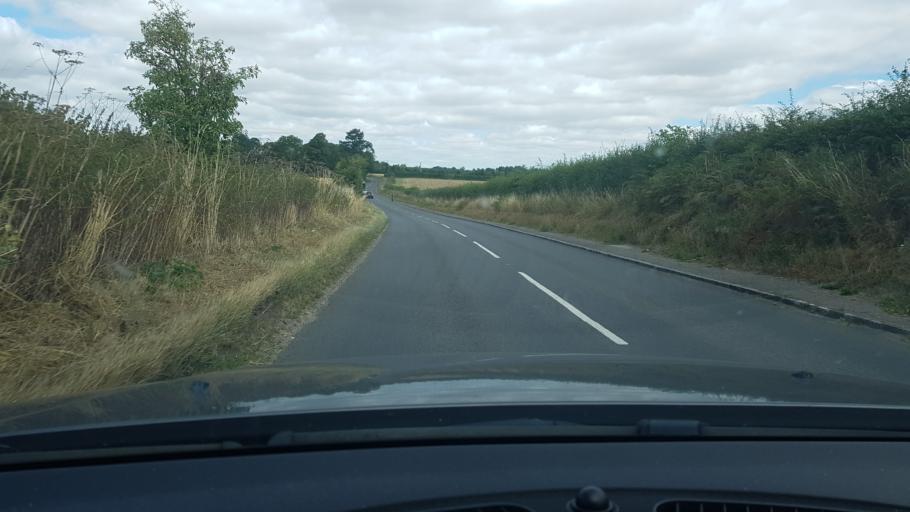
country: GB
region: England
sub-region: West Berkshire
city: Hungerford
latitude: 51.3990
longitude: -1.5256
